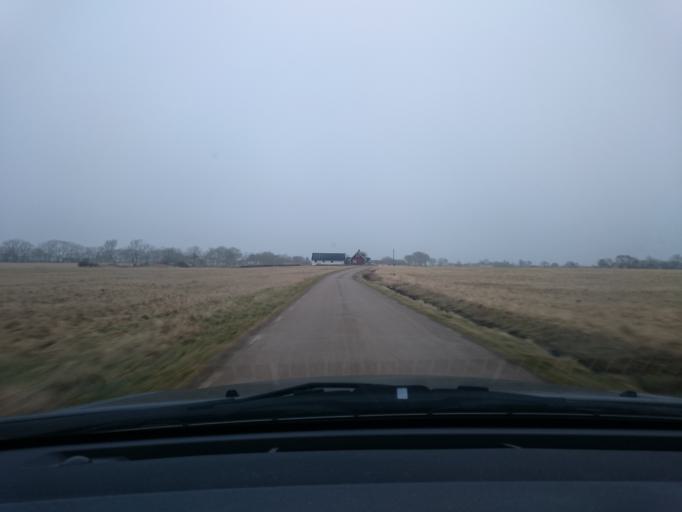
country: SE
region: Skane
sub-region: Angelholms Kommun
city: Vejbystrand
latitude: 56.3445
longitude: 12.7687
